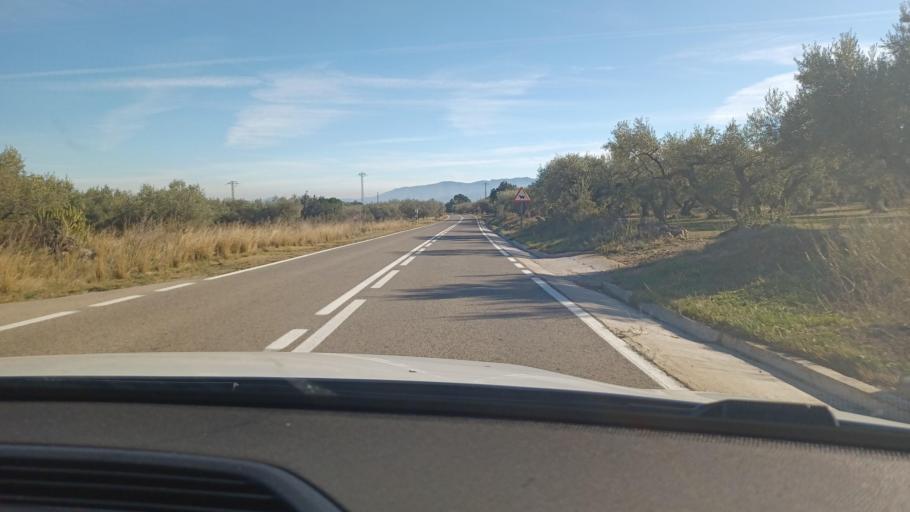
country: ES
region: Catalonia
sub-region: Provincia de Tarragona
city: Mas de Barberans
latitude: 40.7293
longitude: 0.3798
